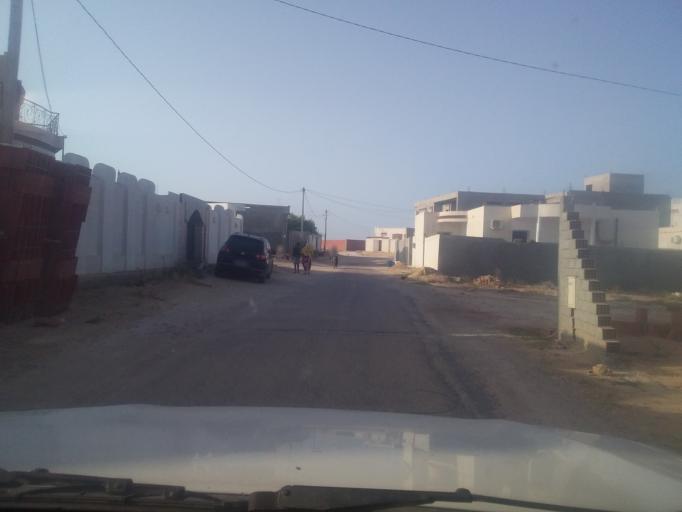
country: TN
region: Qabis
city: Gabes
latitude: 33.6358
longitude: 10.2882
